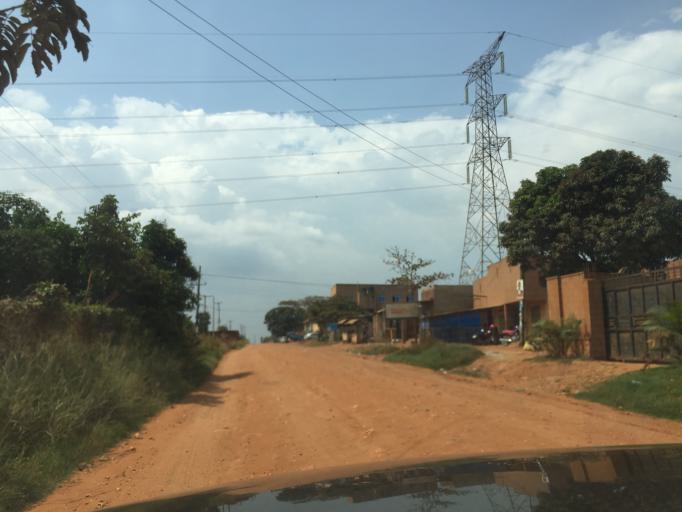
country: UG
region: Central Region
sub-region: Wakiso District
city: Kireka
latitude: 0.4031
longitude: 32.6203
